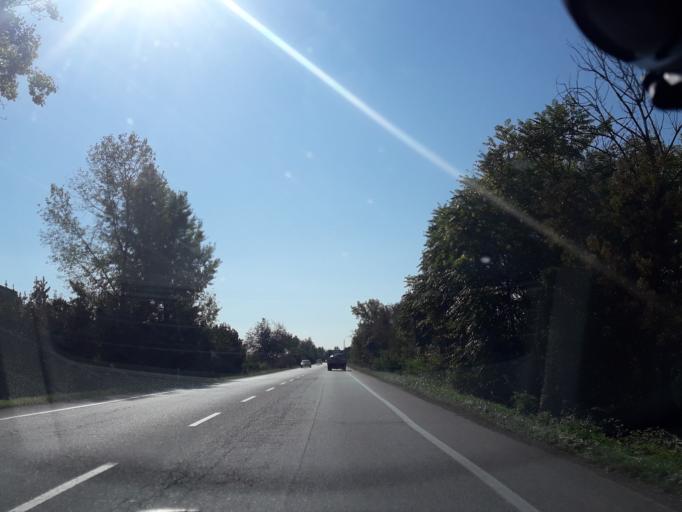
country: IT
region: Friuli Venezia Giulia
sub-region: Provincia di Udine
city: Povoletto
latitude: 46.1073
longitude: 13.2823
